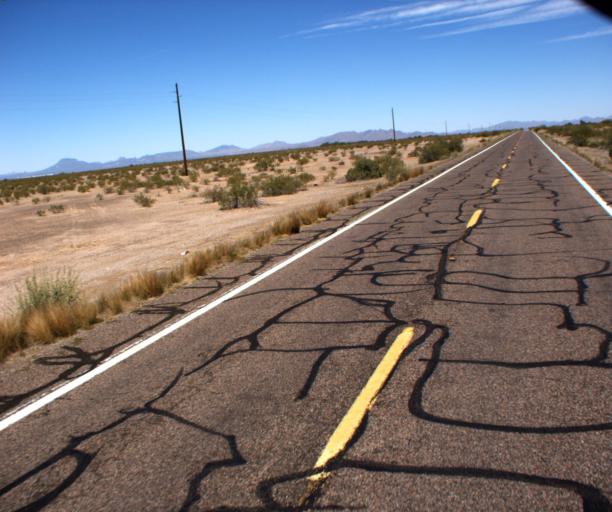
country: US
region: Arizona
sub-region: Maricopa County
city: Gila Bend
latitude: 32.8428
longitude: -112.7756
